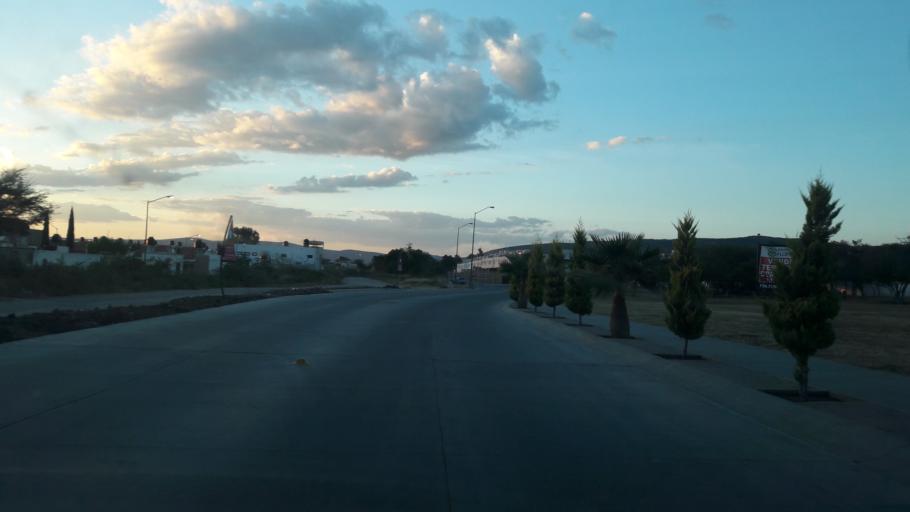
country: MX
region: Guanajuato
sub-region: Leon
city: Medina
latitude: 21.1638
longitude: -101.6333
